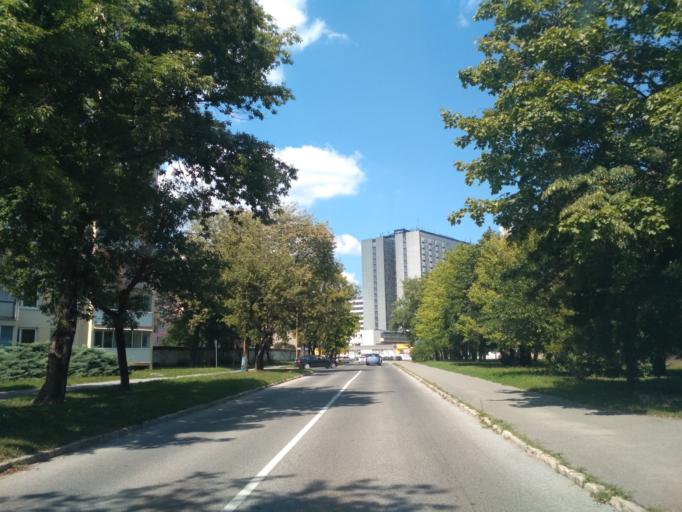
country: SK
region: Kosicky
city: Kosice
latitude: 48.7193
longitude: 21.2397
